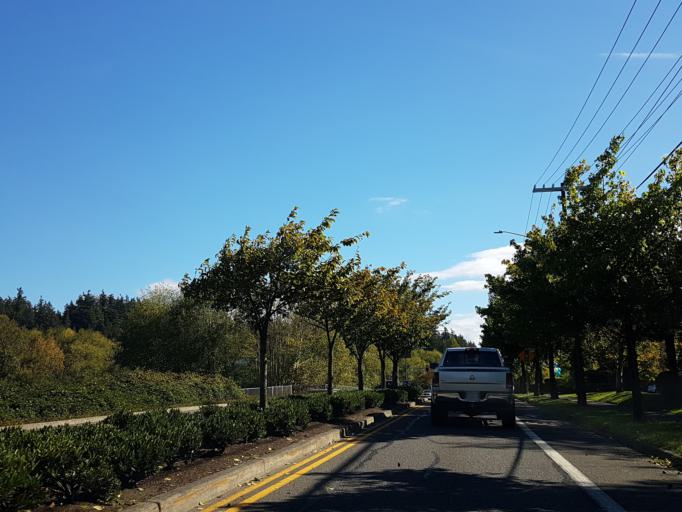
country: US
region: Washington
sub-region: King County
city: Bothell
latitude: 47.7913
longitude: -122.1998
